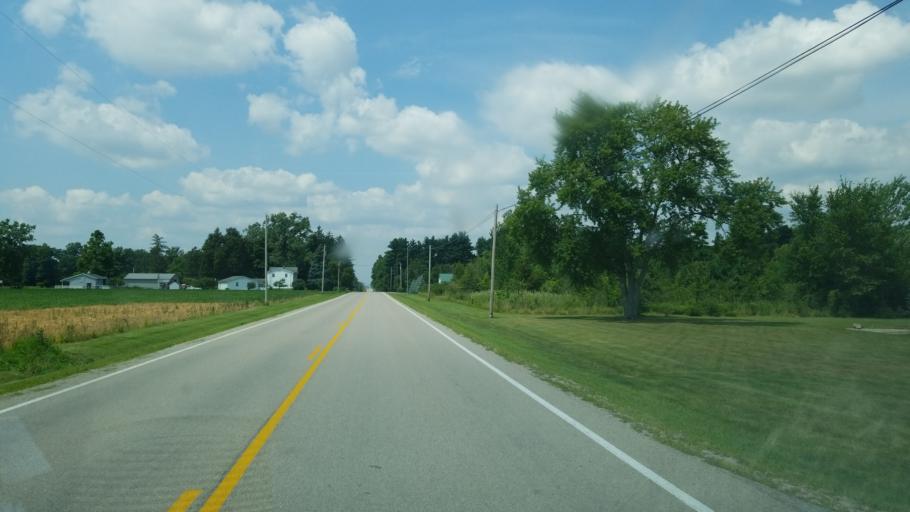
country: US
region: Ohio
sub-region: Defiance County
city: Defiance
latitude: 41.2824
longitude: -84.2707
